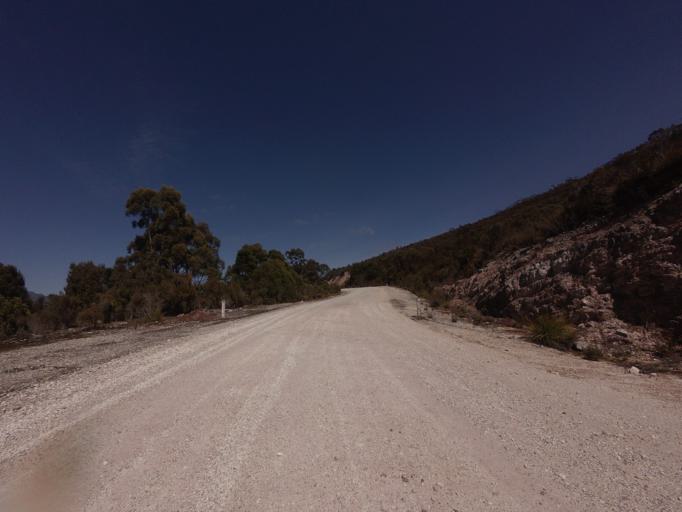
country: AU
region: Tasmania
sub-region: Huon Valley
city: Geeveston
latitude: -43.0361
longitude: 146.2902
